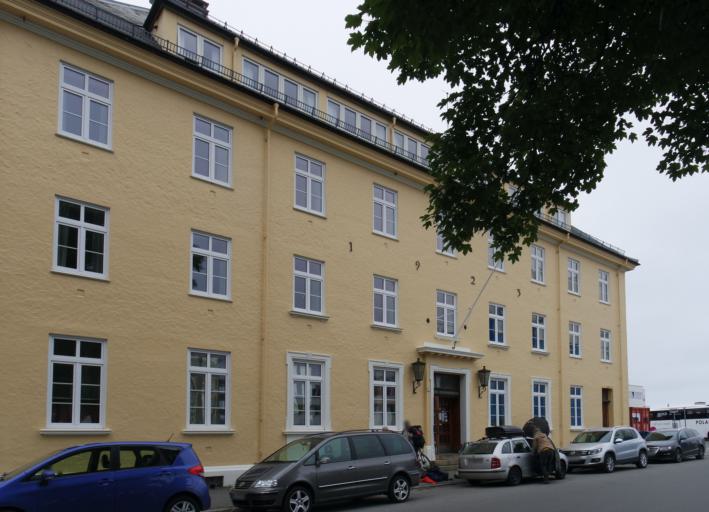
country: NO
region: Nordland
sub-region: Vagan
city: Svolvaer
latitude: 68.2310
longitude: 14.5646
